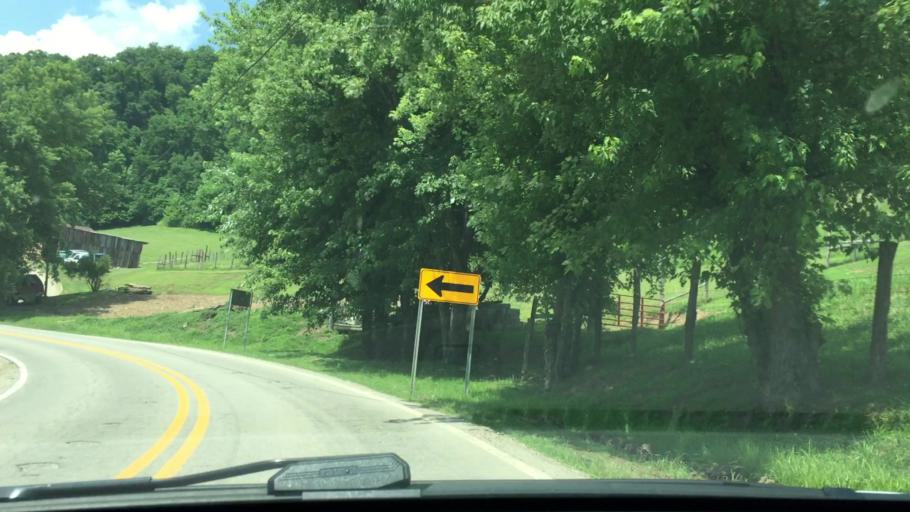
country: US
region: West Virginia
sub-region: Wetzel County
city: New Martinsville
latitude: 39.7027
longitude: -80.8169
